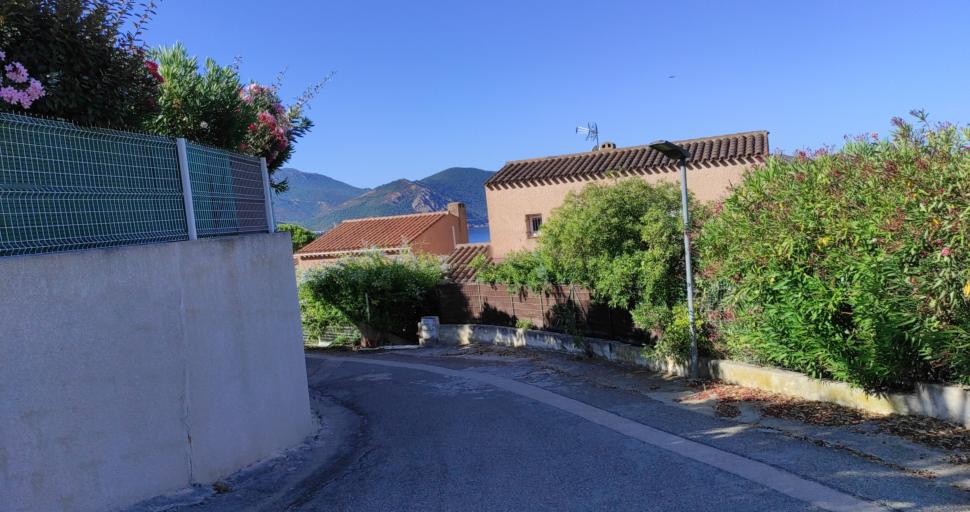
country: FR
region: Corsica
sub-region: Departement de la Corse-du-Sud
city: Alata
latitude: 41.9970
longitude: 8.6699
